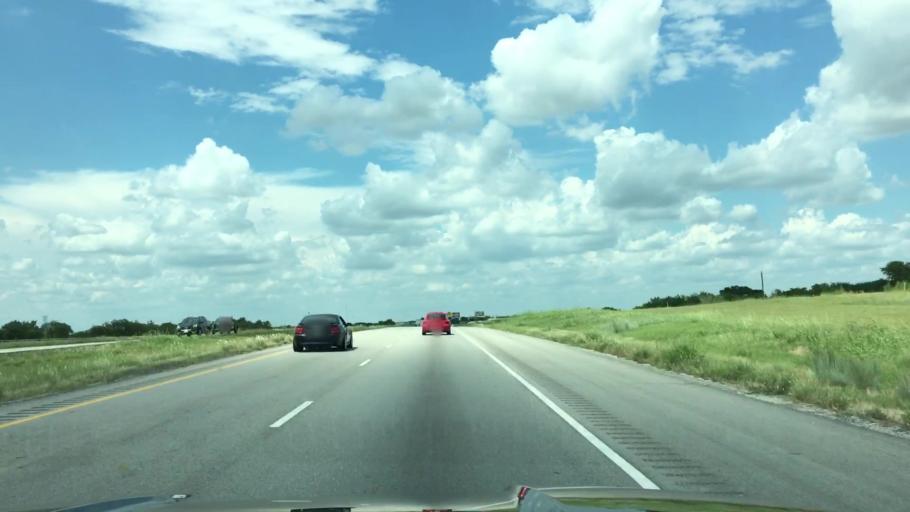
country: US
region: Texas
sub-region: Wise County
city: Newark
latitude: 33.0161
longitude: -97.4400
